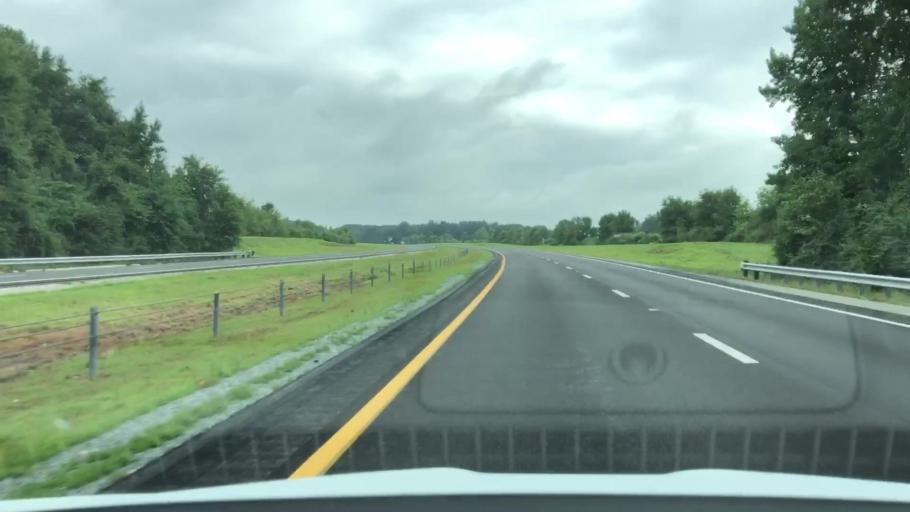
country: US
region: North Carolina
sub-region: Wayne County
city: Fremont
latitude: 35.5168
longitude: -77.9924
